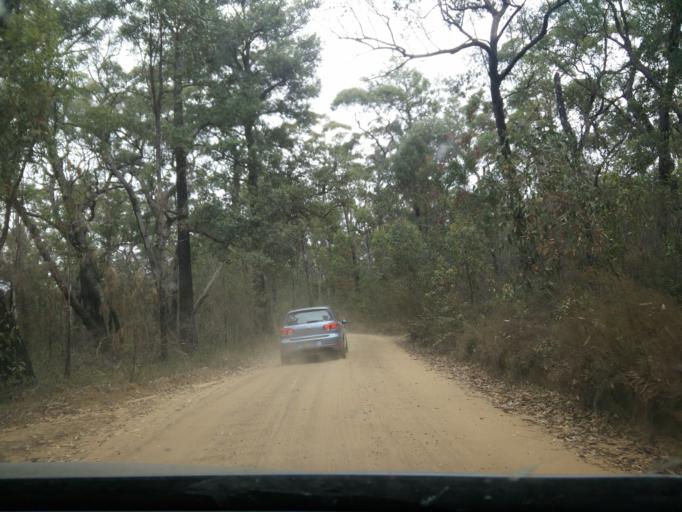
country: AU
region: New South Wales
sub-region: Blue Mountains Municipality
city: Glenbrook
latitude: -33.8070
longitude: 150.5806
